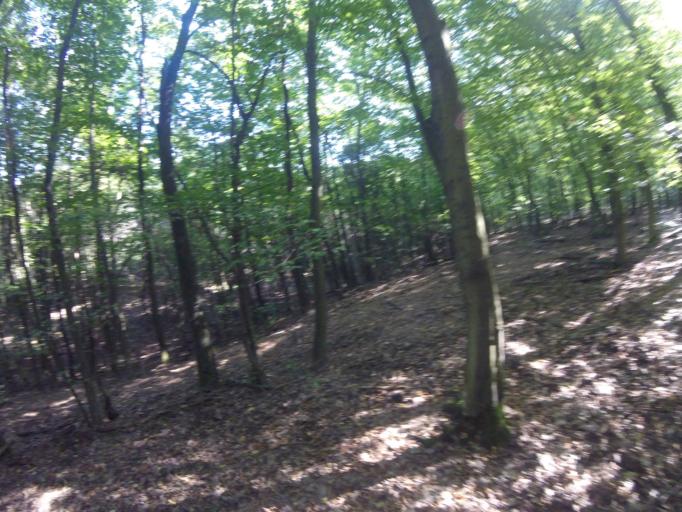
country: HU
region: Nograd
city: Bujak
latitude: 47.8970
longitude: 19.5227
